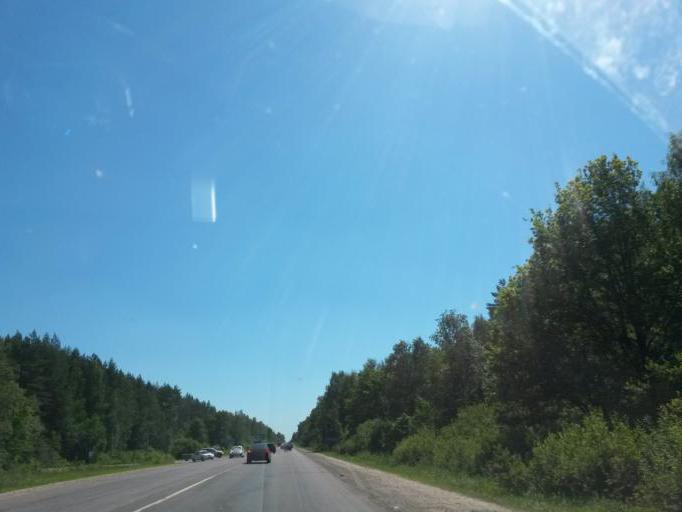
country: RU
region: Moskovskaya
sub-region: Chekhovskiy Rayon
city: Chekhov
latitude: 55.0896
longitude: 37.4420
